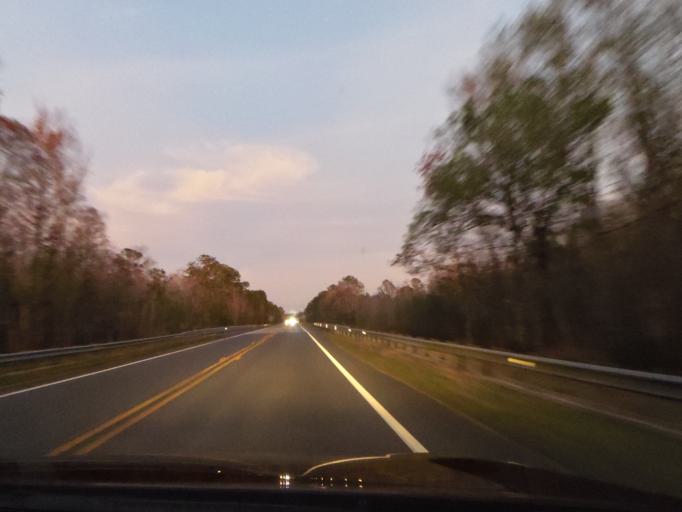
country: US
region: Florida
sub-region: Volusia County
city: De Leon Springs
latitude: 29.2266
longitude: -81.3120
